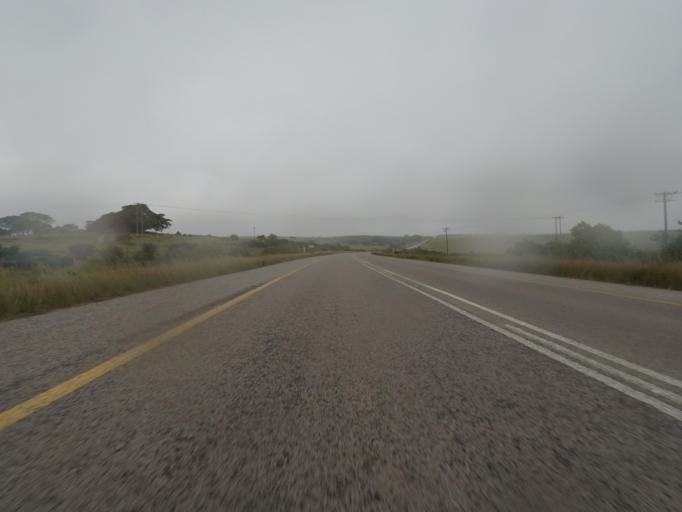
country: ZA
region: Eastern Cape
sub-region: Cacadu District Municipality
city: Grahamstown
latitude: -33.6423
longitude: 26.3714
